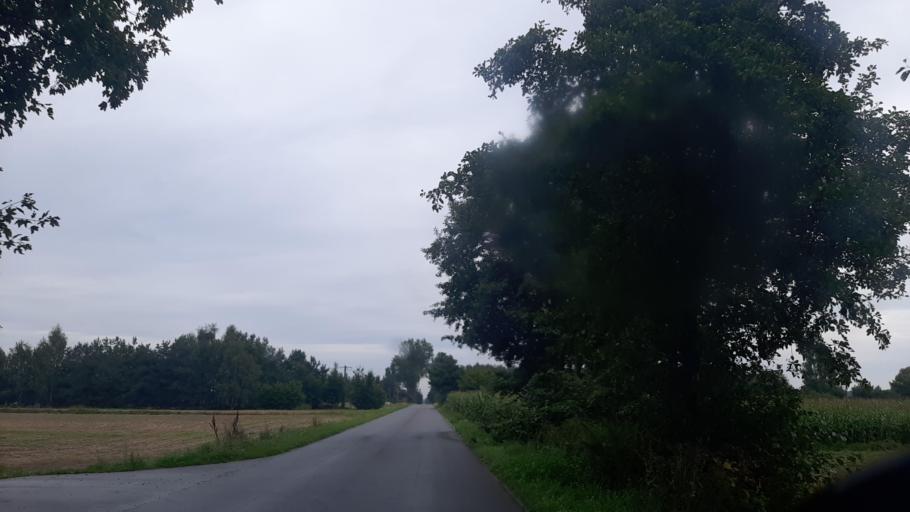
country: PL
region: Lublin Voivodeship
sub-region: Powiat lubartowski
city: Kamionka
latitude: 51.4697
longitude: 22.4289
